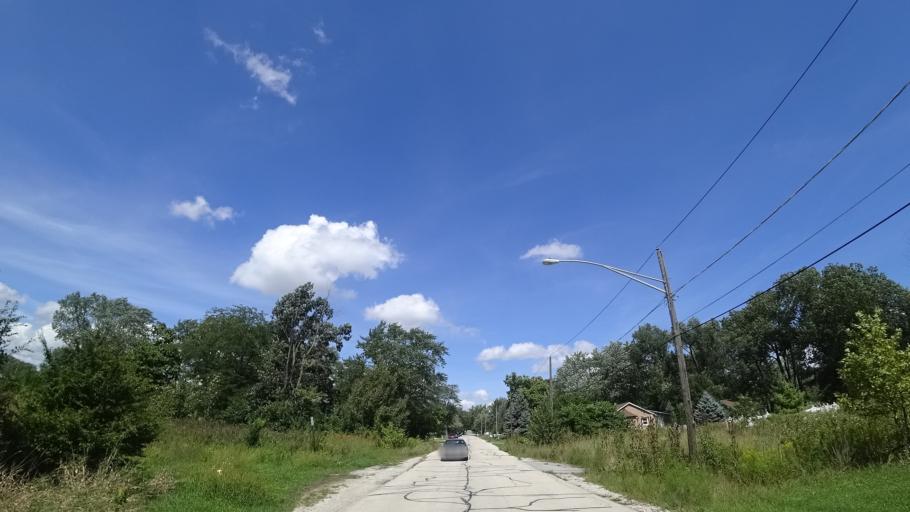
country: US
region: Illinois
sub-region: Cook County
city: Tinley Park
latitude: 41.5675
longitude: -87.7886
